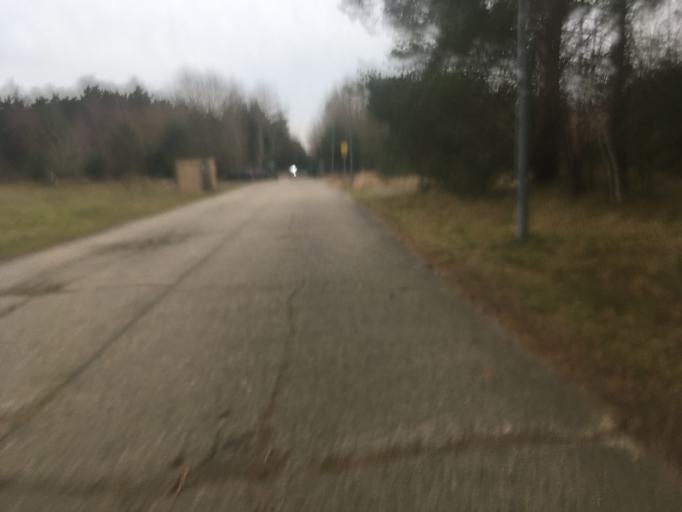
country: DE
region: Mecklenburg-Vorpommern
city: Ostseebad Binz
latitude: 54.4556
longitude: 13.5678
